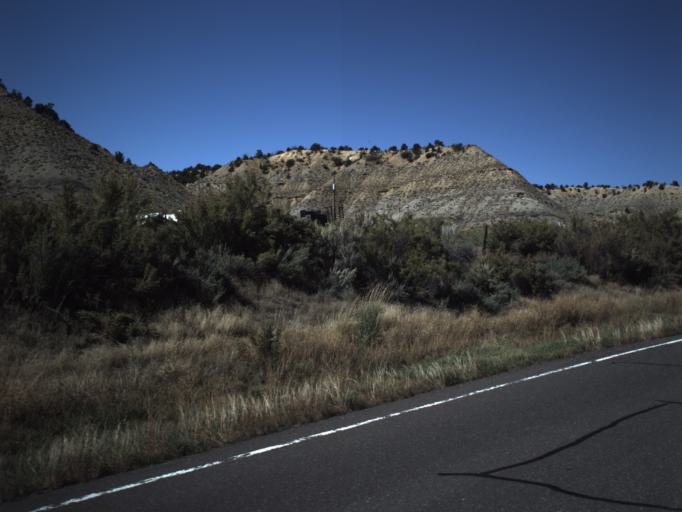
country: US
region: Utah
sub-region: Garfield County
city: Panguitch
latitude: 37.5967
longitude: -112.0617
